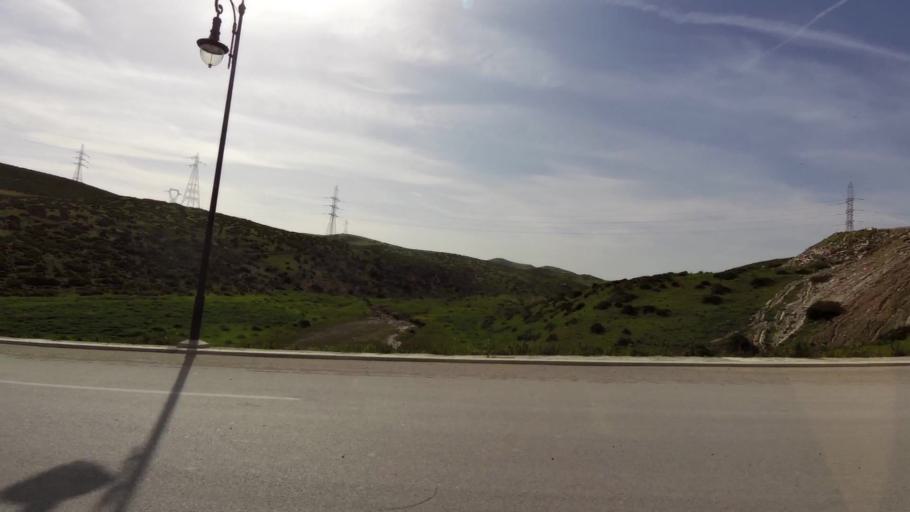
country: MA
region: Tanger-Tetouan
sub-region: Tanger-Assilah
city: Tangier
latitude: 35.7184
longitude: -5.7689
